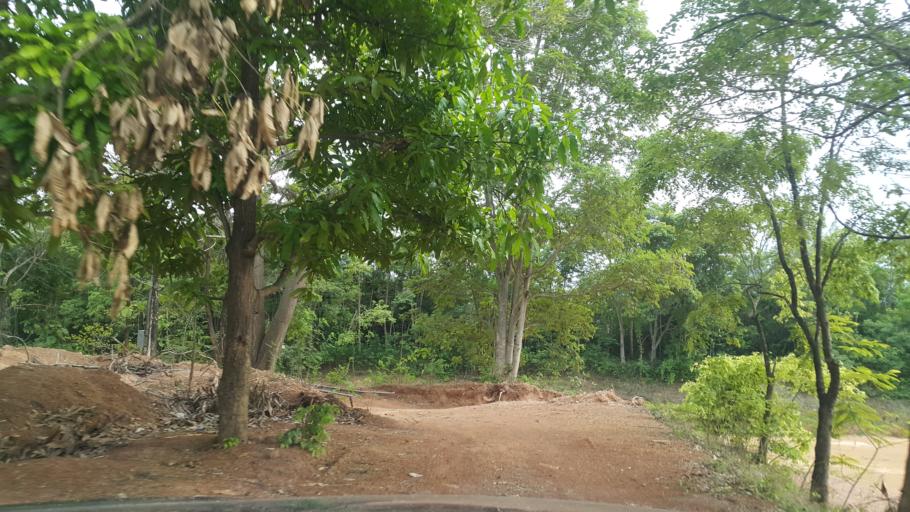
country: TH
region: Chiang Mai
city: Mae On
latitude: 18.7285
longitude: 99.2275
